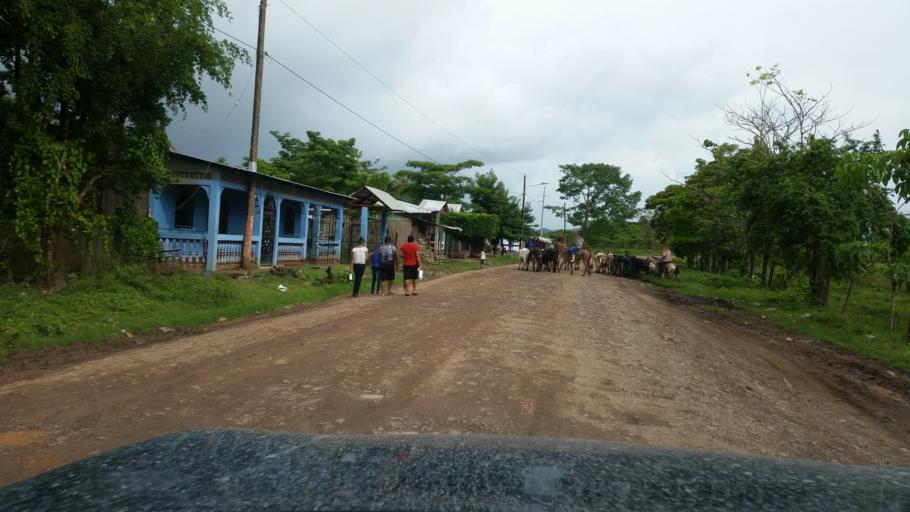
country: NI
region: Atlantico Norte (RAAN)
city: Siuna
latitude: 13.4308
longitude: -84.8526
